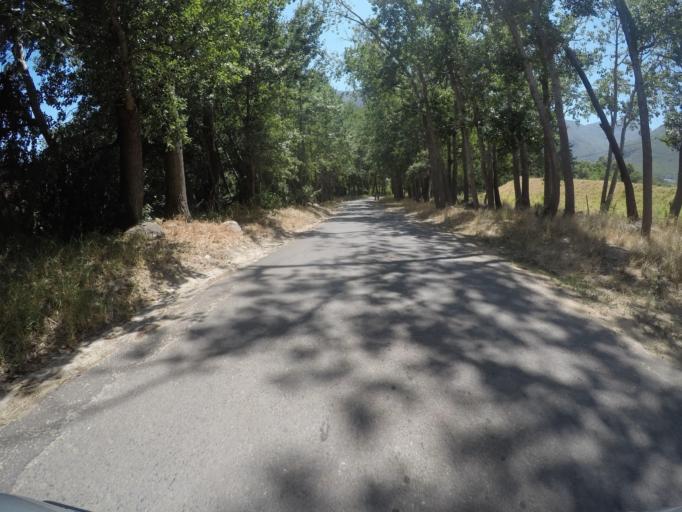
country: ZA
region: Western Cape
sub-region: Cape Winelands District Municipality
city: Stellenbosch
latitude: -33.9958
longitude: 18.8762
